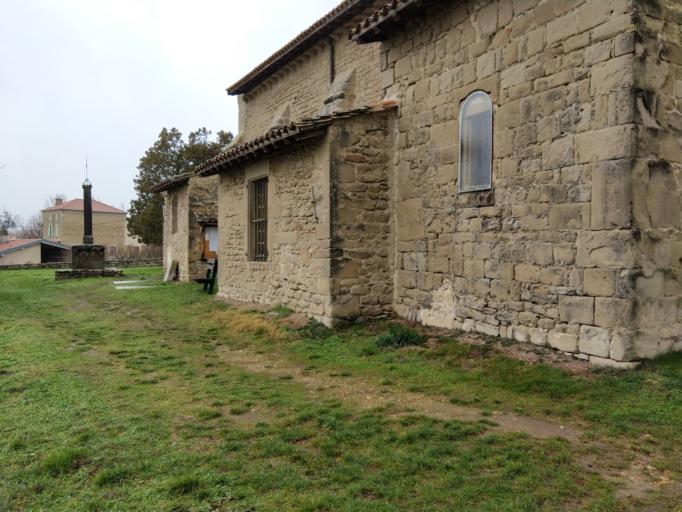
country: FR
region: Rhone-Alpes
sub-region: Departement de la Drome
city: Saint-Uze
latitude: 45.1986
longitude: 4.9079
